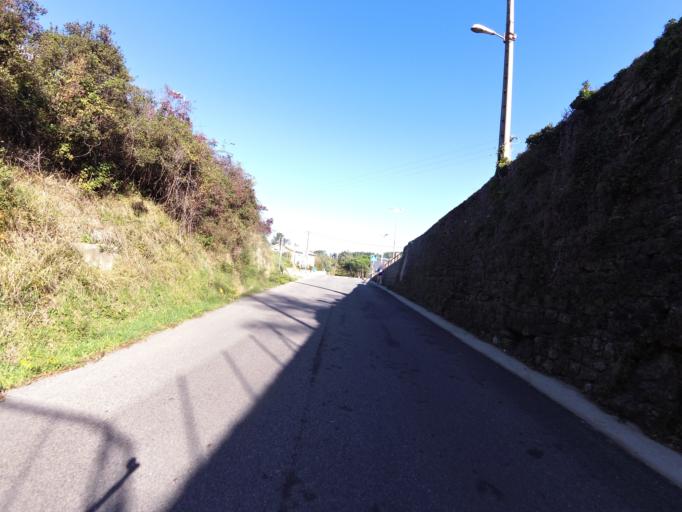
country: FR
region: Rhone-Alpes
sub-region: Departement de l'Ardeche
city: Largentiere
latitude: 44.5427
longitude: 4.2986
